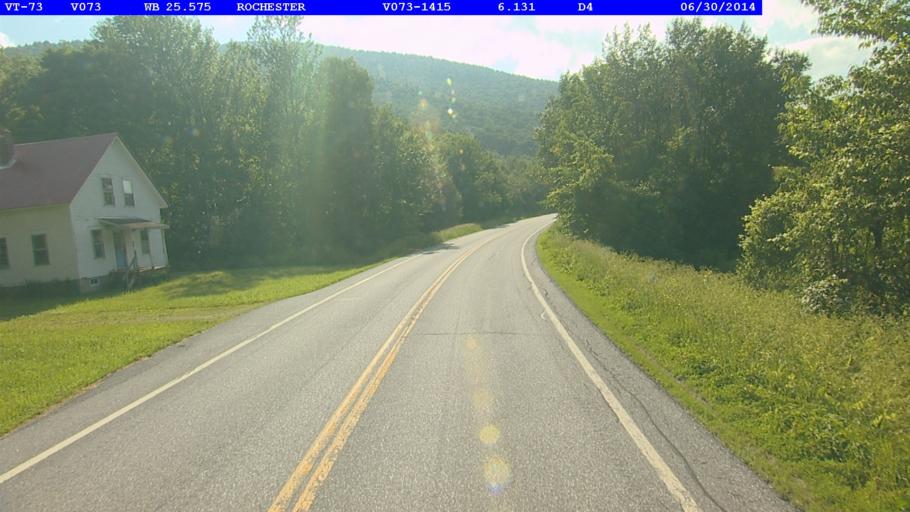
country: US
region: Vermont
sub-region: Orange County
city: Randolph
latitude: 43.8480
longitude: -72.8541
